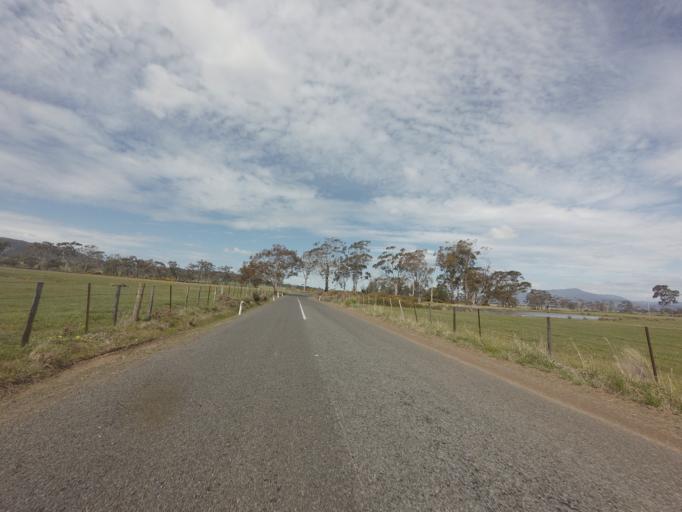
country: AU
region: Tasmania
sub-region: Northern Midlands
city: Longford
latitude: -41.7367
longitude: 147.2002
